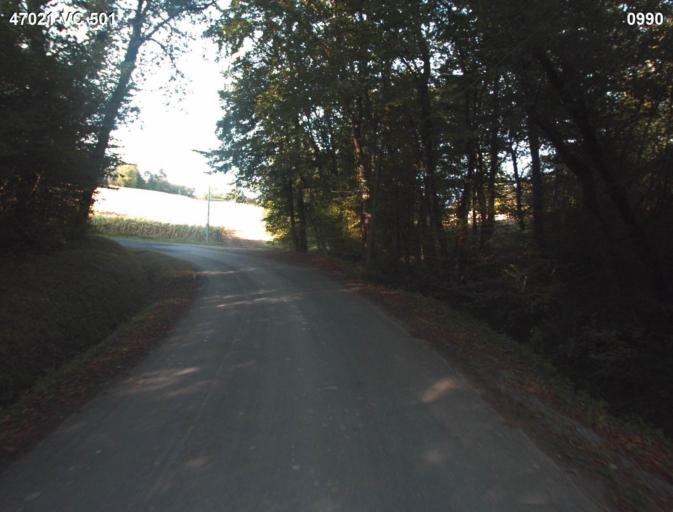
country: FR
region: Aquitaine
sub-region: Departement du Lot-et-Garonne
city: Barbaste
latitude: 44.1862
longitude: 0.2557
